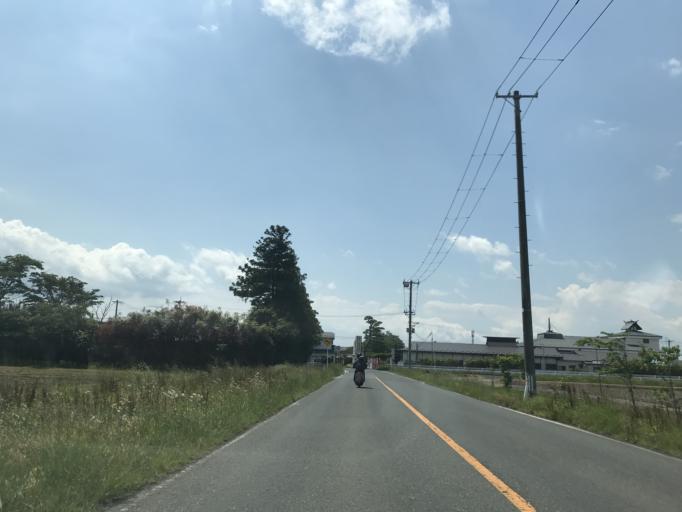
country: JP
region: Miyagi
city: Kogota
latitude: 38.5871
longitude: 141.0315
